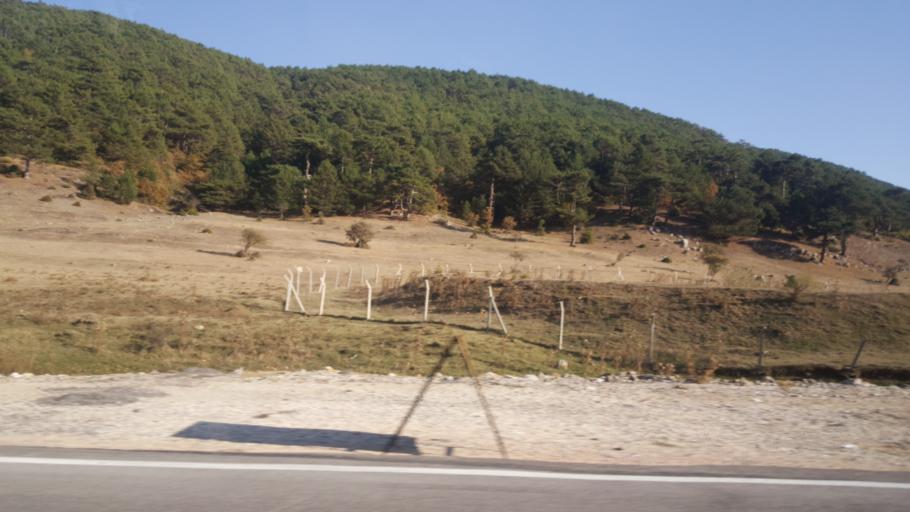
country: TR
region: Afyonkarahisar
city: Ihsaniye
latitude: 39.1014
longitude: 30.5793
